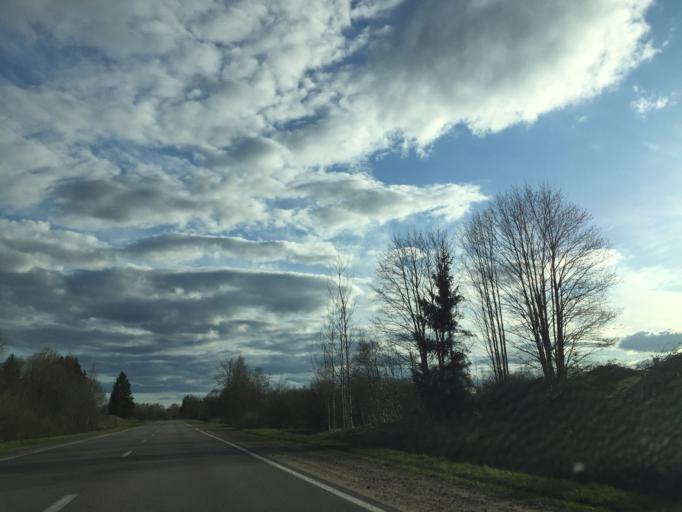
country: LV
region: Rezekne
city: Rezekne
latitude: 56.5741
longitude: 27.3759
